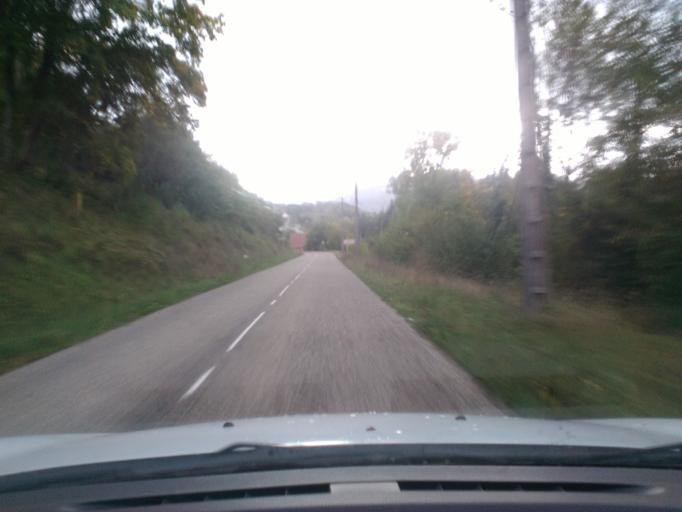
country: FR
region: Lorraine
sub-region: Departement des Vosges
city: Saint-Die-des-Vosges
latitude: 48.3144
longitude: 6.9619
